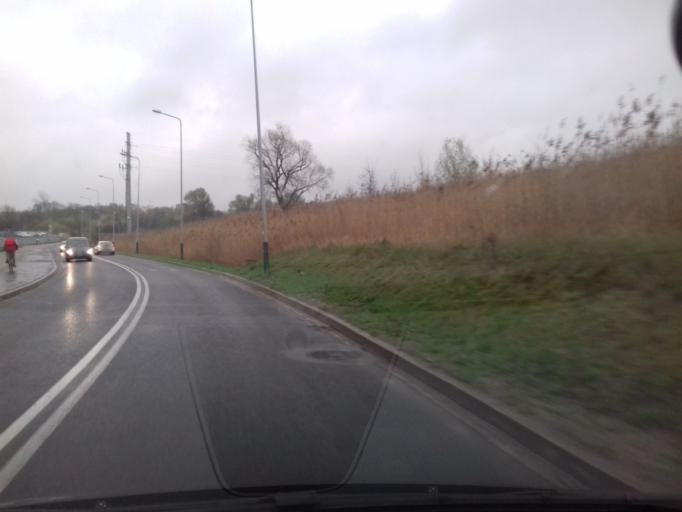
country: PL
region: Lesser Poland Voivodeship
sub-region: Krakow
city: Krakow
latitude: 50.0259
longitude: 19.9496
